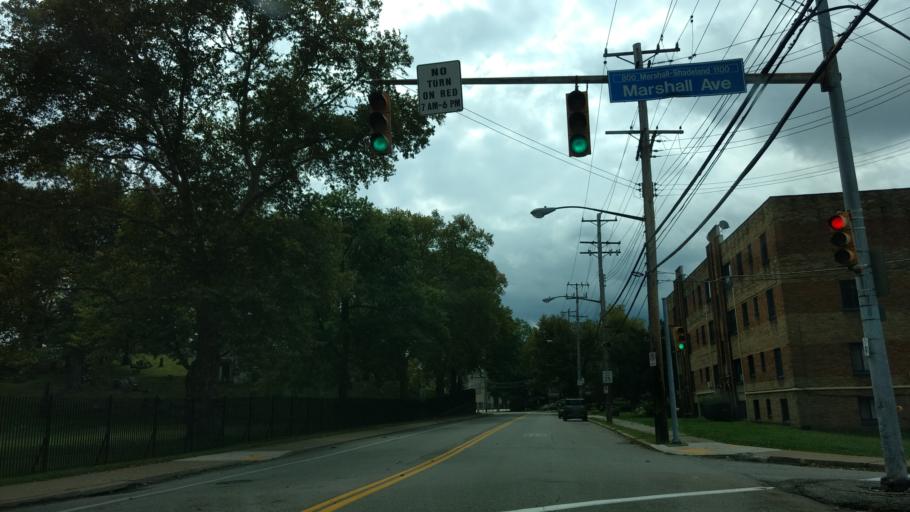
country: US
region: Pennsylvania
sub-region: Allegheny County
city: Bellevue
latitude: 40.4668
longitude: -80.0250
